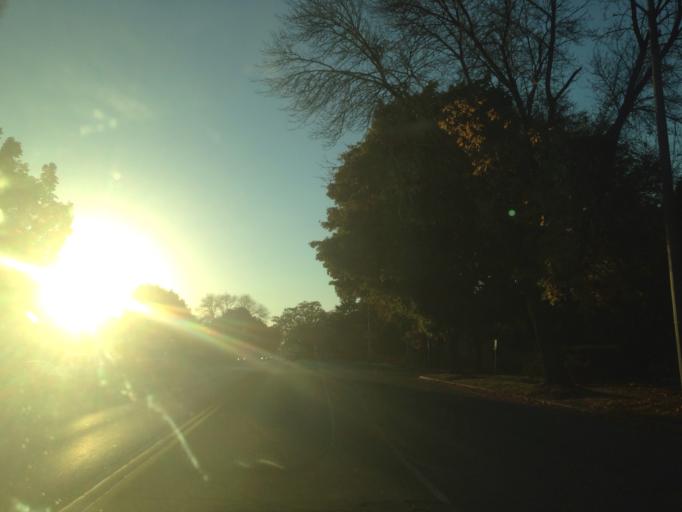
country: US
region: Wisconsin
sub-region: Milwaukee County
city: Wauwatosa
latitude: 43.0361
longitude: -87.9950
